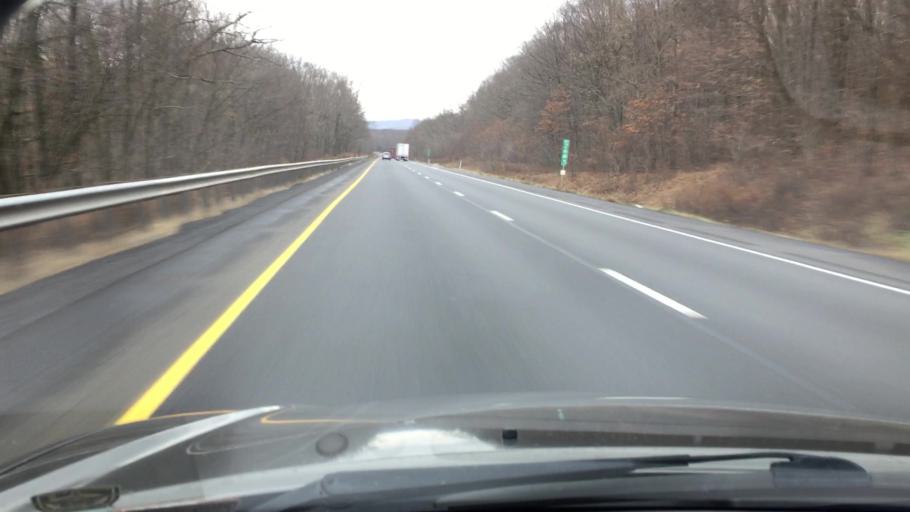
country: US
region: Pennsylvania
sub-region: Luzerne County
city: Freeland
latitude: 41.0620
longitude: -75.8864
